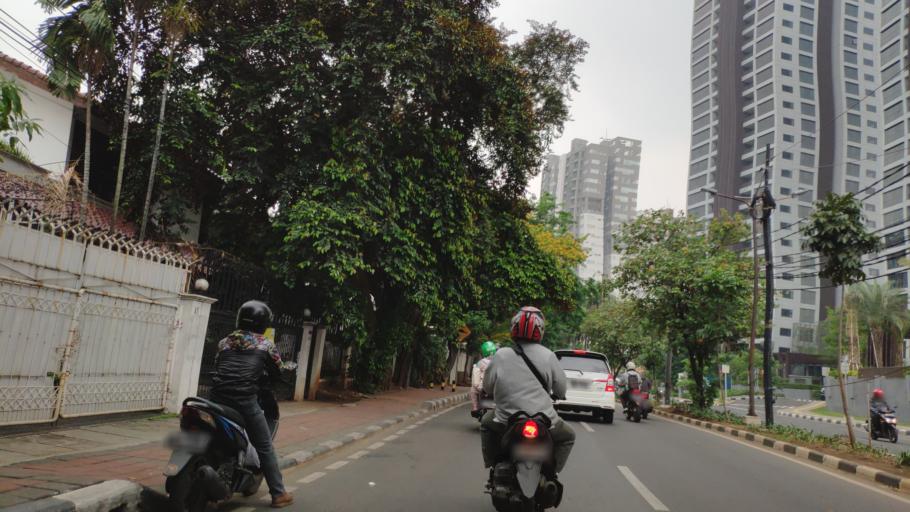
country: ID
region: Jakarta Raya
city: Jakarta
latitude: -6.2457
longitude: 106.7862
